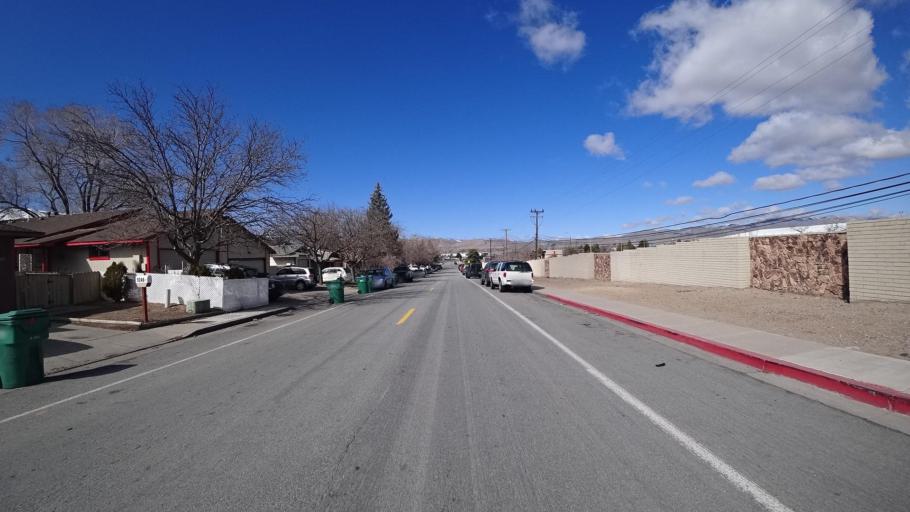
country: US
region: Nevada
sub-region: Washoe County
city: Lemmon Valley
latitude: 39.6540
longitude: -119.8786
